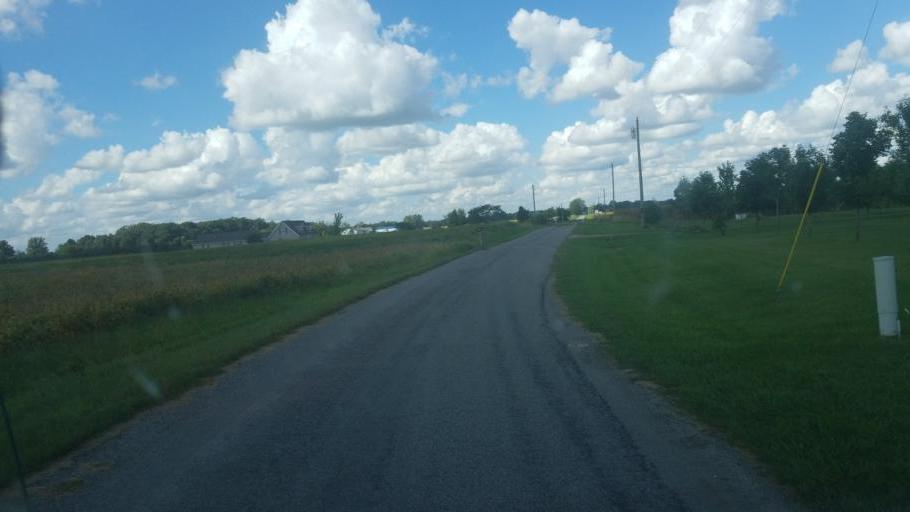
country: US
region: Ohio
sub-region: Hardin County
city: Kenton
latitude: 40.4768
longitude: -83.4980
